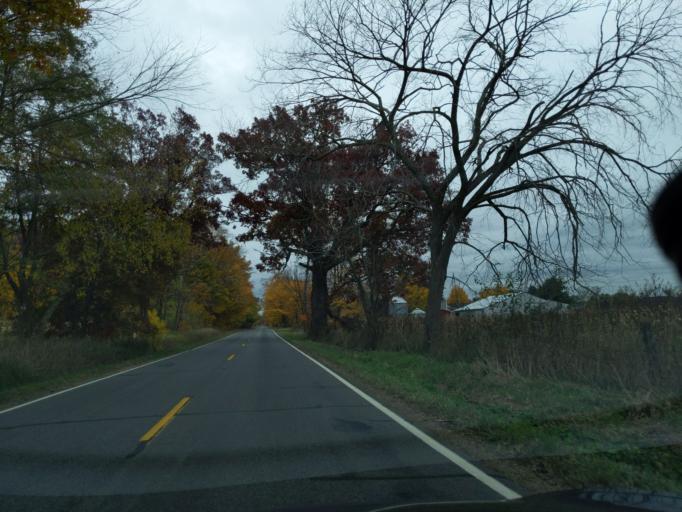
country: US
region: Michigan
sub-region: Jackson County
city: Spring Arbor
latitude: 42.3180
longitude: -84.6004
